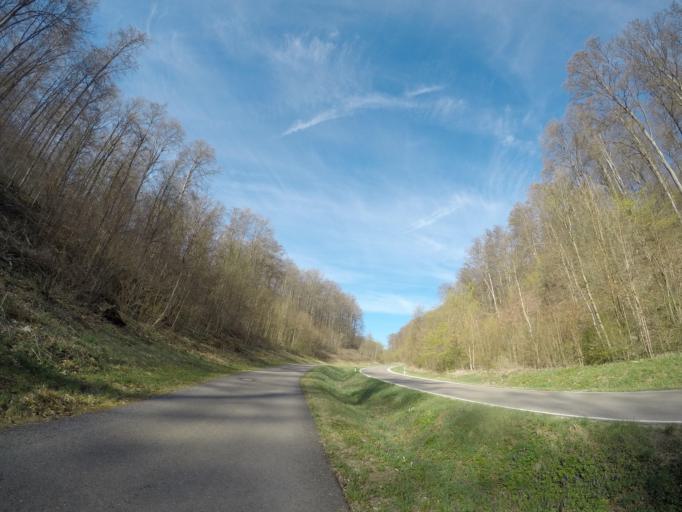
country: DE
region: Baden-Wuerttemberg
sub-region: Tuebingen Region
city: Allmendingen
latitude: 48.3470
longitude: 9.6756
